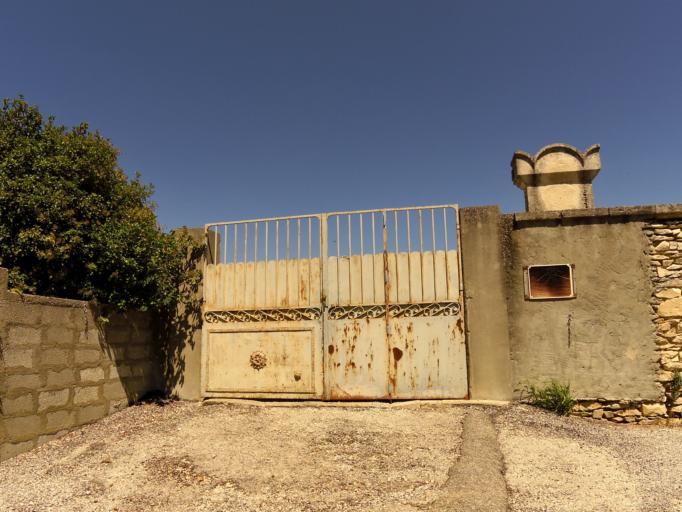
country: FR
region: Languedoc-Roussillon
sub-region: Departement du Gard
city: Clarensac
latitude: 43.8289
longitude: 4.2161
